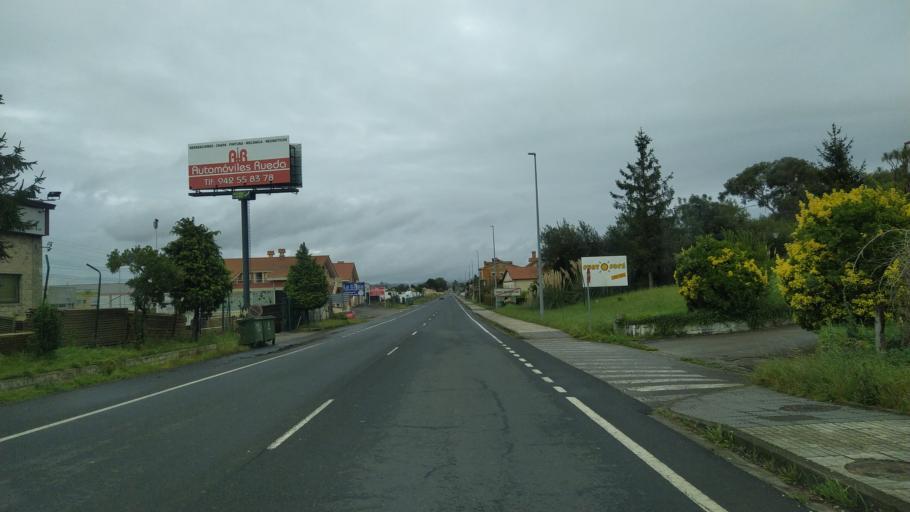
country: ES
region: Cantabria
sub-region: Provincia de Cantabria
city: El Astillero
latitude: 43.3938
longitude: -3.8008
